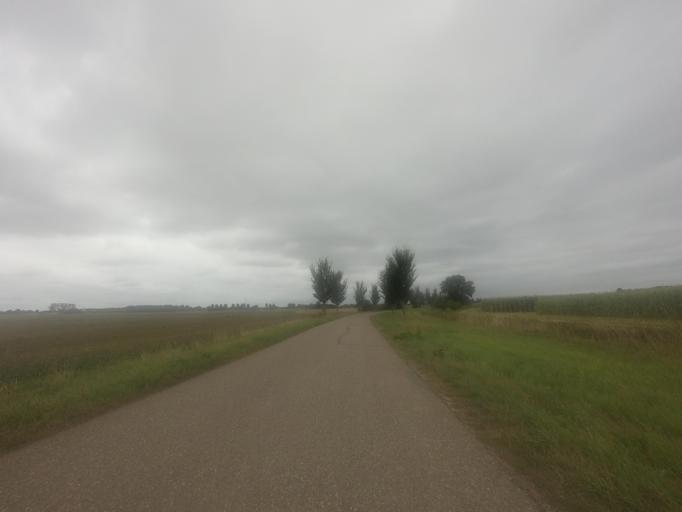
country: NL
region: North Brabant
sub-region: Gemeente Grave
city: Grave
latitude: 51.7853
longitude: 5.7467
